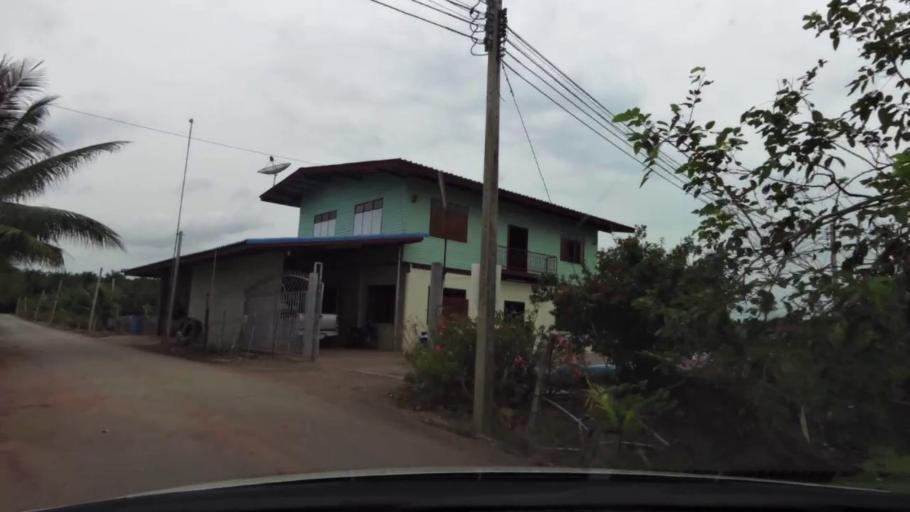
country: TH
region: Samut Sakhon
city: Ban Phaeo
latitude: 13.6004
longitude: 100.0296
